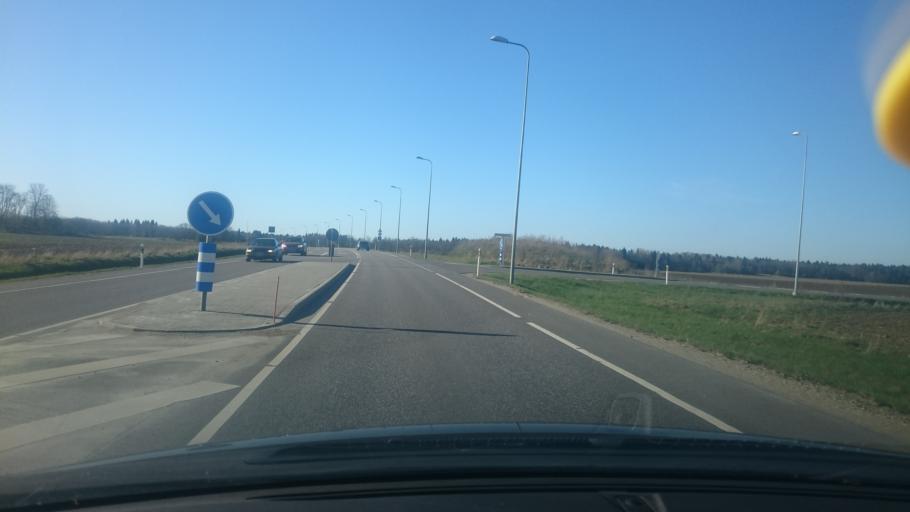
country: EE
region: Harju
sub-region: Kiili vald
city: Kiili
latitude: 59.3392
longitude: 24.8225
